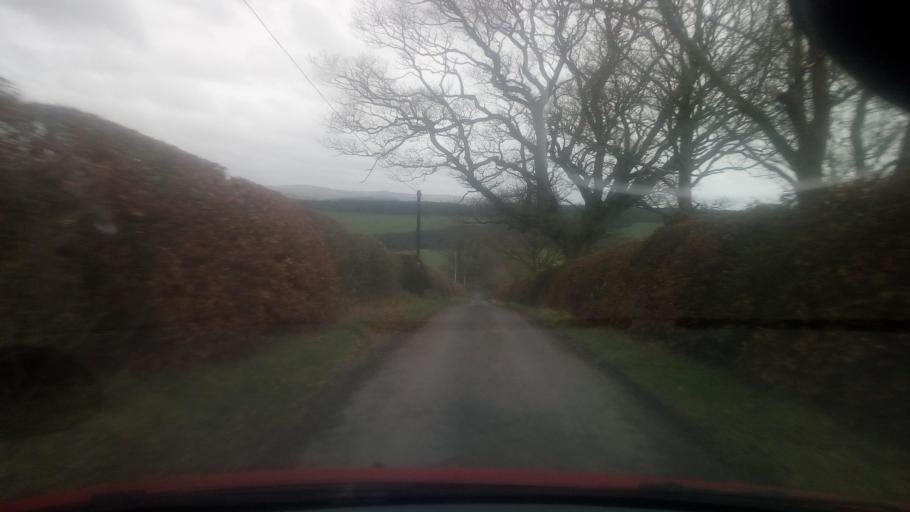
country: GB
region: Scotland
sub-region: The Scottish Borders
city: Jedburgh
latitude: 55.4618
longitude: -2.5171
